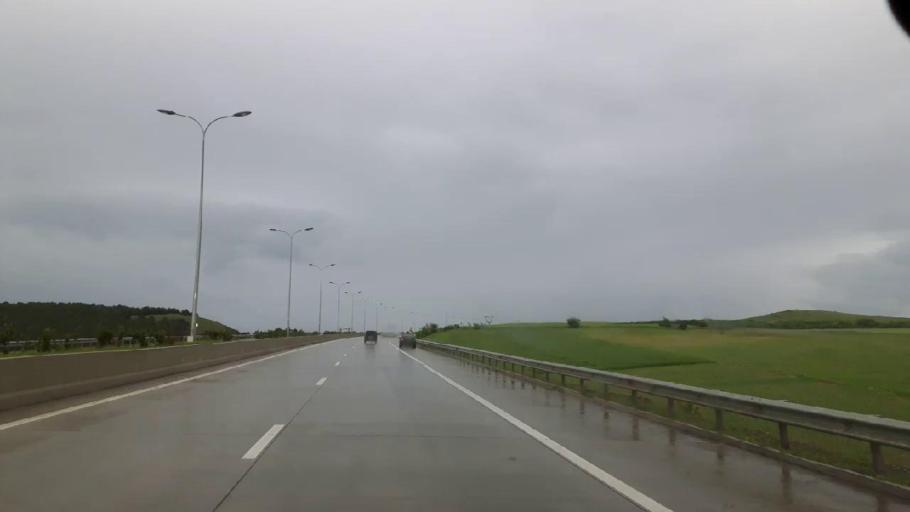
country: GE
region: Shida Kartli
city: Gori
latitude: 42.0200
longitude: 44.0074
